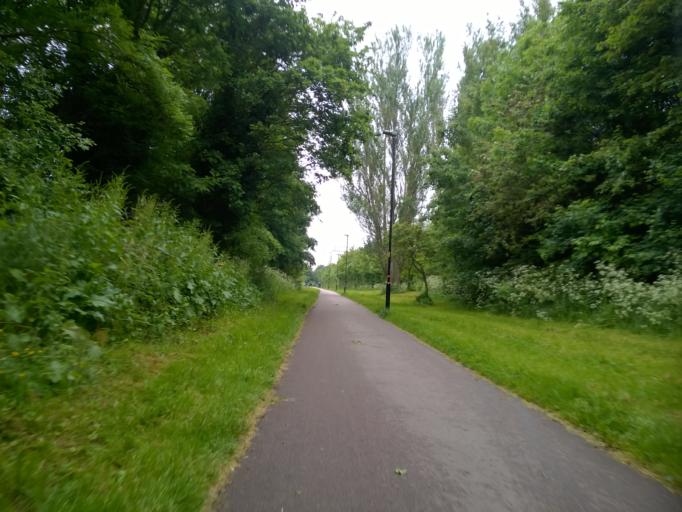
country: GB
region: England
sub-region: City of Leicester
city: Leicester
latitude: 52.6226
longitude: -1.1489
